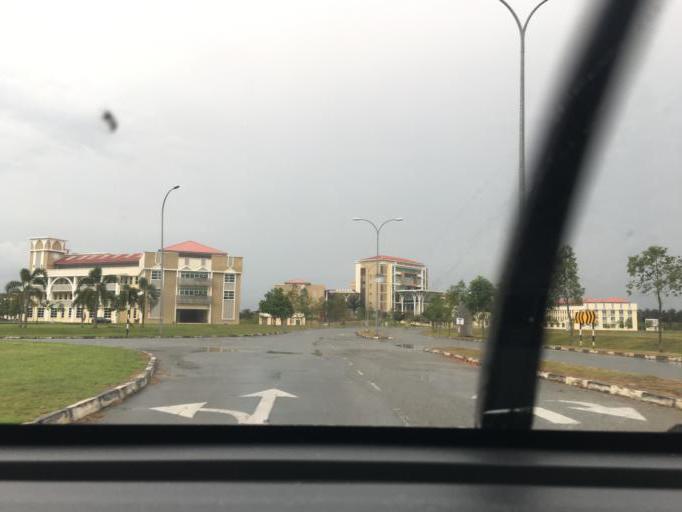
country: MY
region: Kedah
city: Sungai Petani
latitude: 5.5861
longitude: 100.6414
